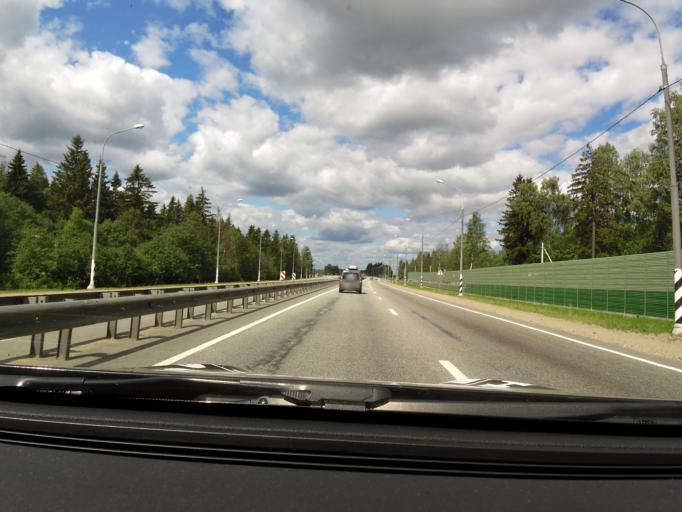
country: RU
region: Tverskaya
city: Torzhok
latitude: 57.0002
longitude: 35.1528
